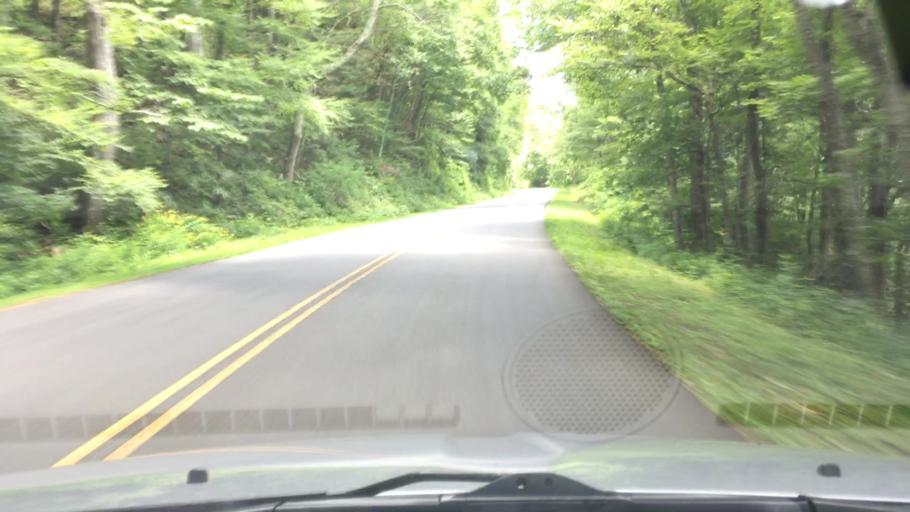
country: US
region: North Carolina
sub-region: Buncombe County
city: Swannanoa
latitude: 35.6762
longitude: -82.4397
